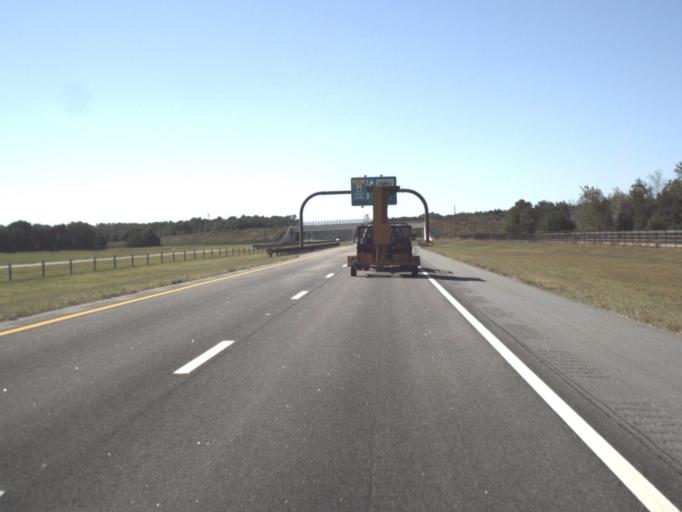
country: US
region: Florida
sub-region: Pasco County
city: Shady Hills
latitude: 28.4047
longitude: -82.5148
